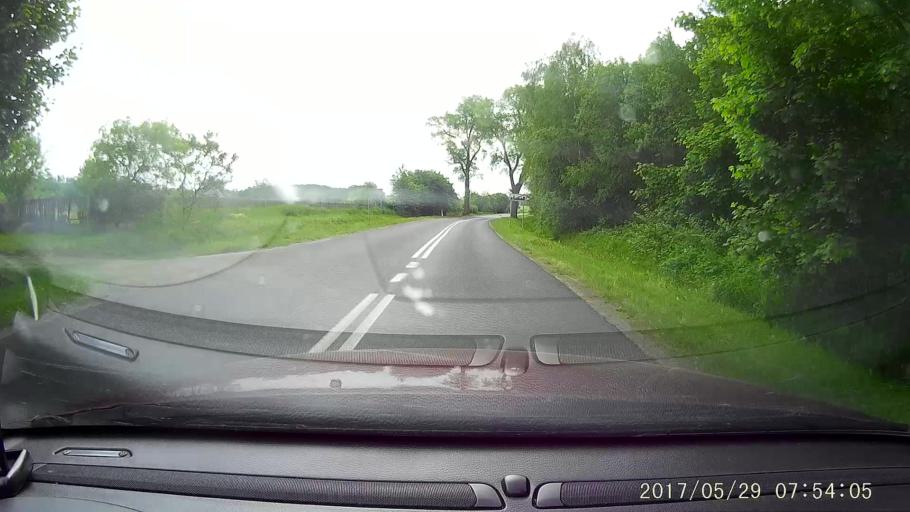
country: PL
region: Lower Silesian Voivodeship
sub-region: Powiat zlotoryjski
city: Olszanica
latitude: 51.2166
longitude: 15.7402
